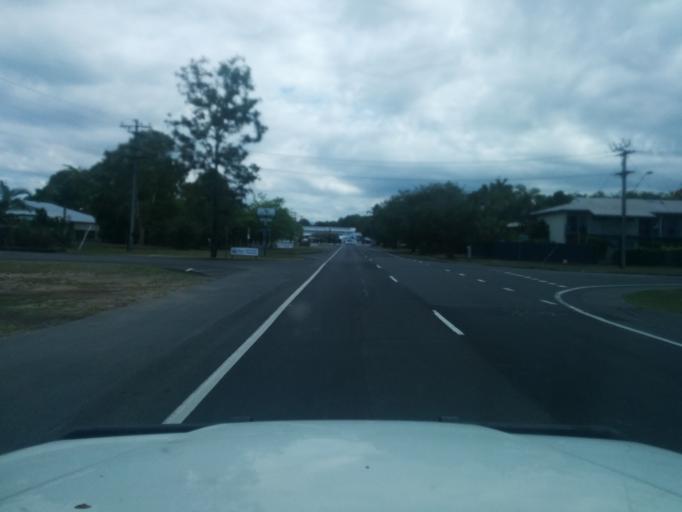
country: AU
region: Queensland
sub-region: Cairns
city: Cairns
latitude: -16.9118
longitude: 145.7500
